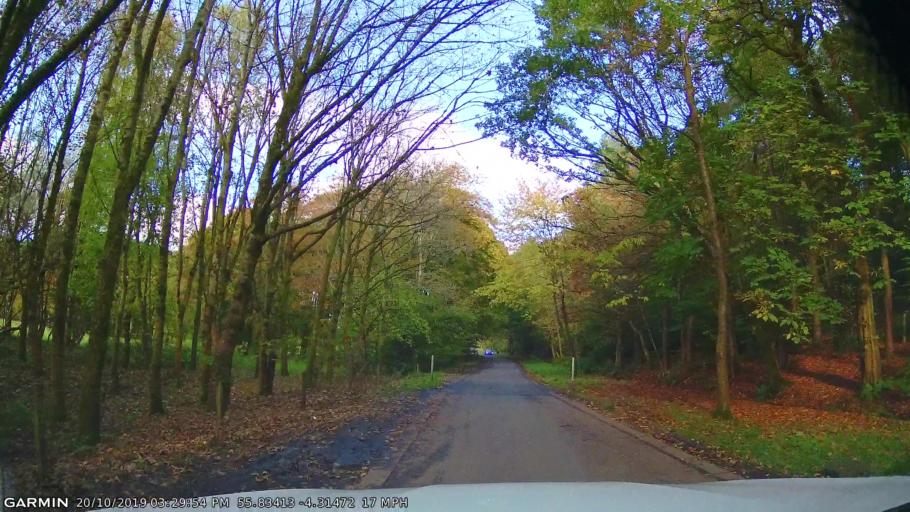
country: GB
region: Scotland
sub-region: East Renfrewshire
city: Giffnock
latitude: 55.8341
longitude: -4.3147
